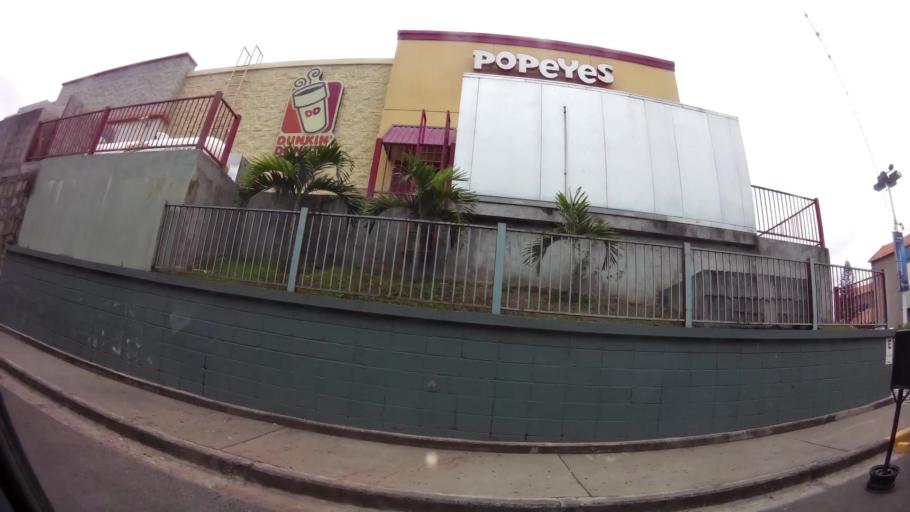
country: HN
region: Francisco Morazan
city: Tegucigalpa
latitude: 14.0777
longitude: -87.1859
